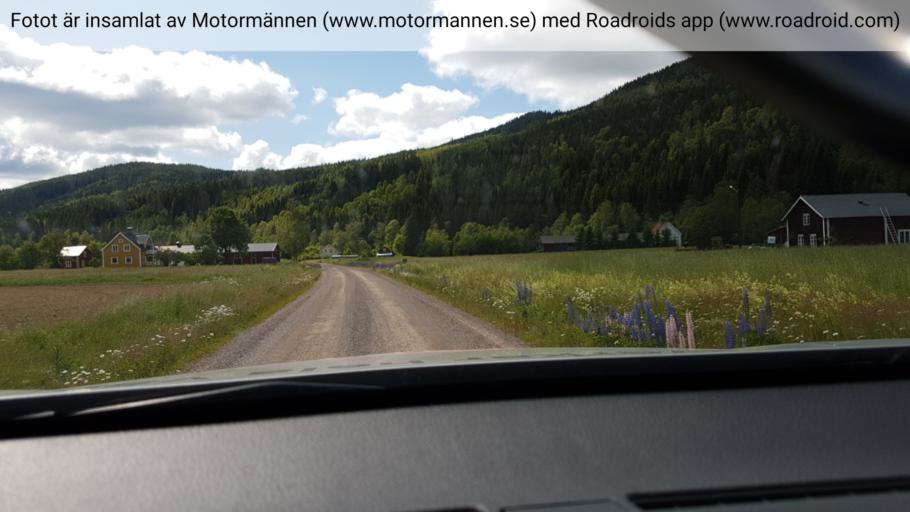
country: SE
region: Vaermland
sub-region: Hagfors Kommun
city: Ekshaerad
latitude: 60.3143
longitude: 13.3629
